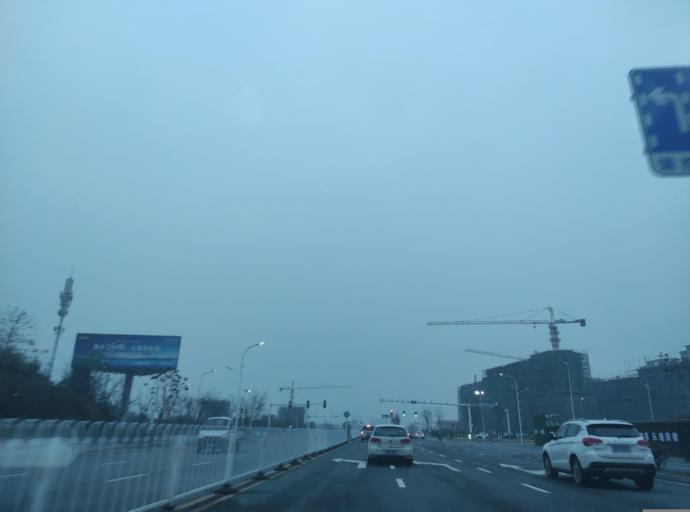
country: CN
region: Jiangxi Sheng
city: Pingxiang
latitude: 27.6710
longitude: 113.8539
